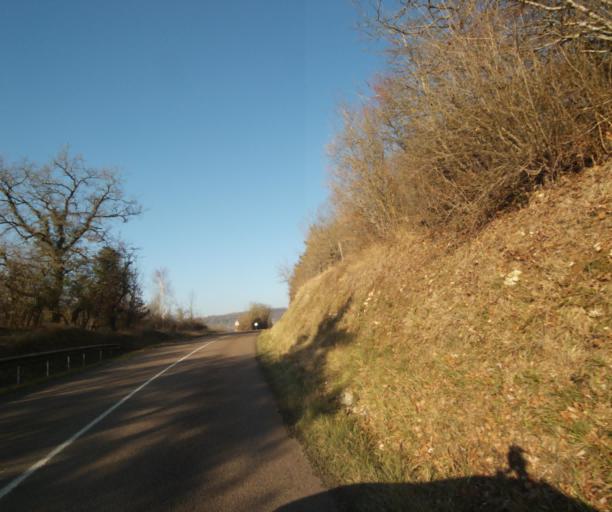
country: FR
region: Champagne-Ardenne
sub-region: Departement de la Haute-Marne
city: Chevillon
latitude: 48.5153
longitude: 5.1187
